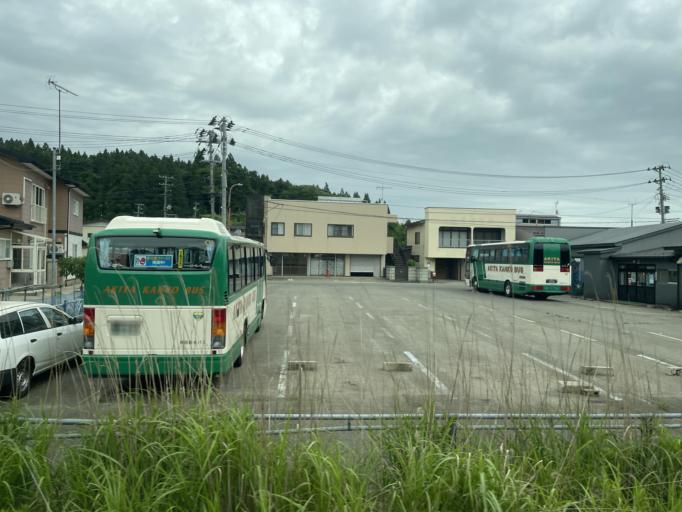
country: JP
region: Akita
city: Tenno
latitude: 39.9052
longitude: 139.8628
